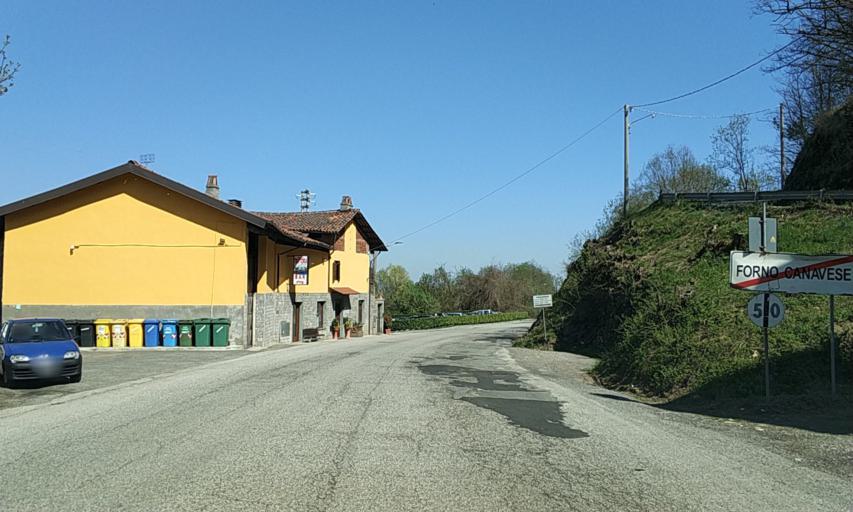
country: IT
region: Piedmont
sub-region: Provincia di Torino
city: Forno Canavese
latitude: 45.3373
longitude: 7.6059
